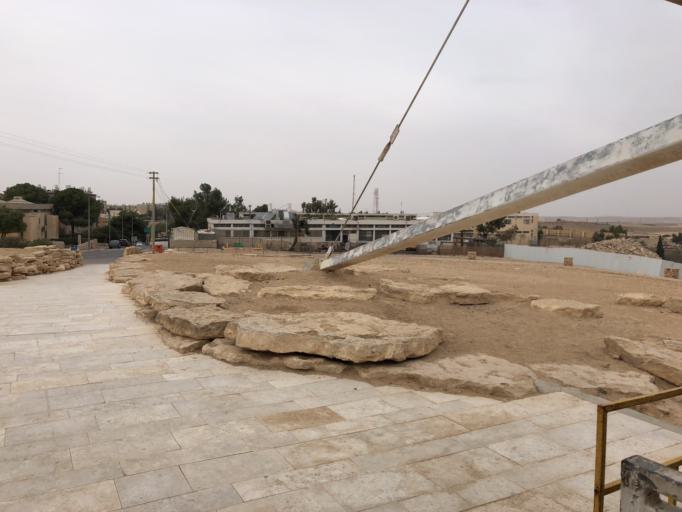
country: IL
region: Southern District
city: Mitzpe Ramon
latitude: 30.6062
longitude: 34.8044
